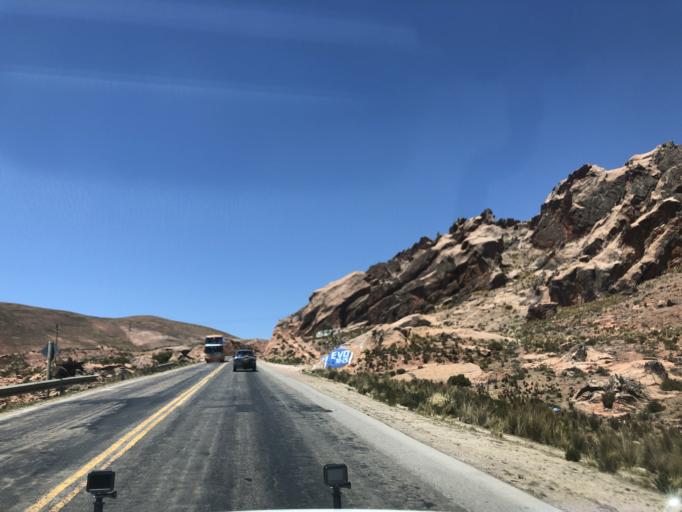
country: BO
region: Cochabamba
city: Colchani
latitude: -17.6888
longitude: -66.7088
